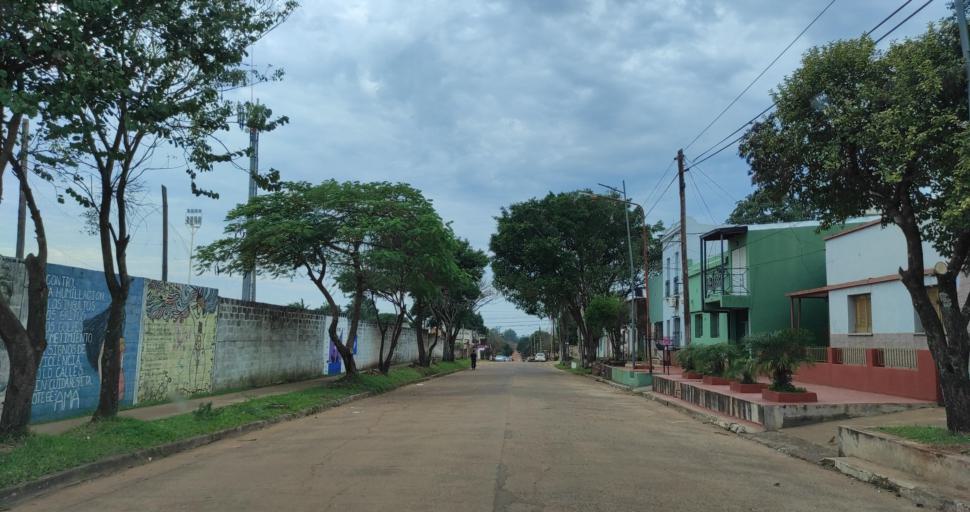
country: AR
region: Corrientes
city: Santo Tome
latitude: -28.5542
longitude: -56.0406
